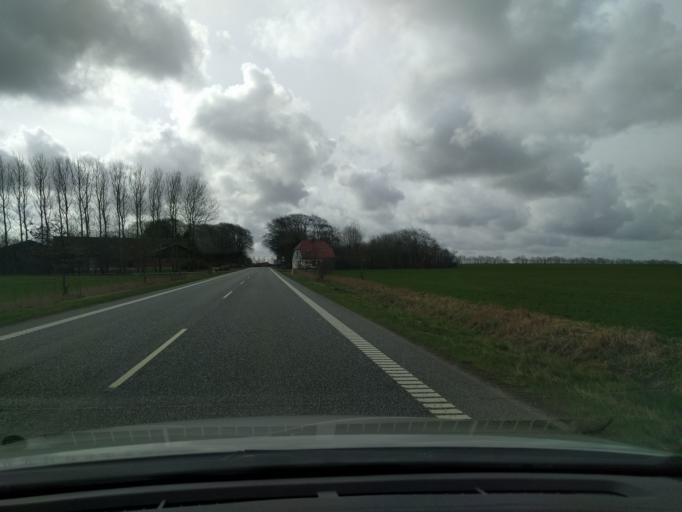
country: DK
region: South Denmark
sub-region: Tonder Kommune
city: Toftlund
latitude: 55.1439
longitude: 9.0149
